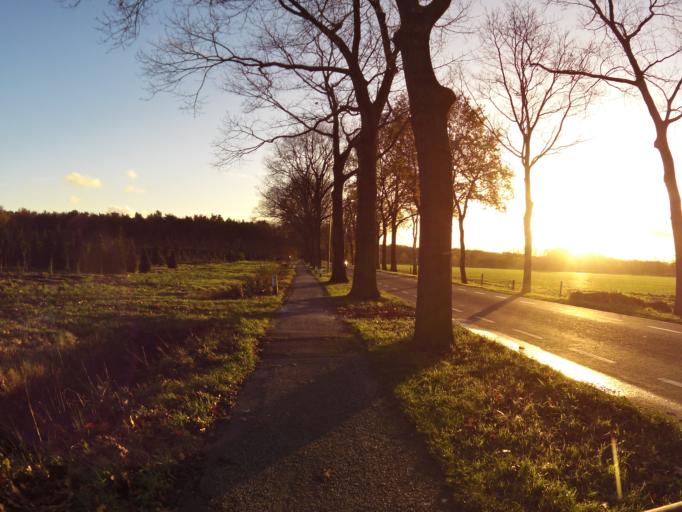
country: NL
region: North Brabant
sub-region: Gemeente Waalwijk
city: Waalwijk
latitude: 51.6615
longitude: 5.0725
